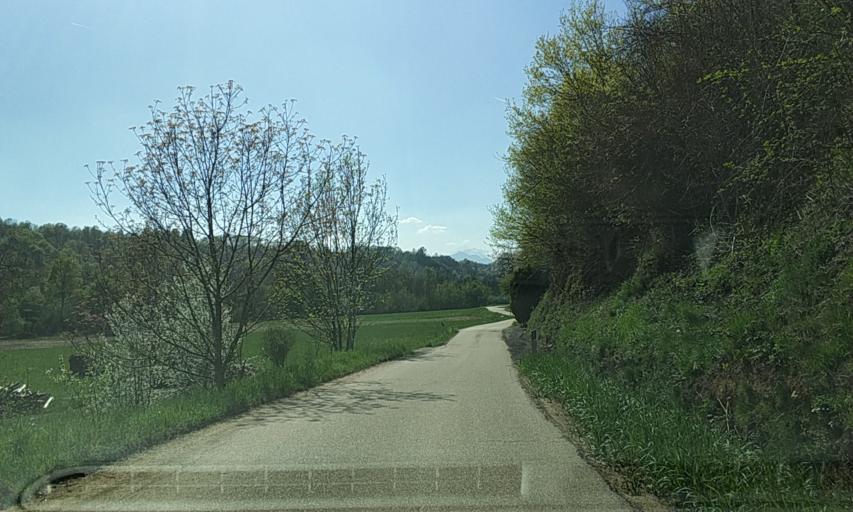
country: IT
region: Piedmont
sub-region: Provincia di Torino
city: Vauda Canavese Superiore
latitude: 45.2852
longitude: 7.6044
